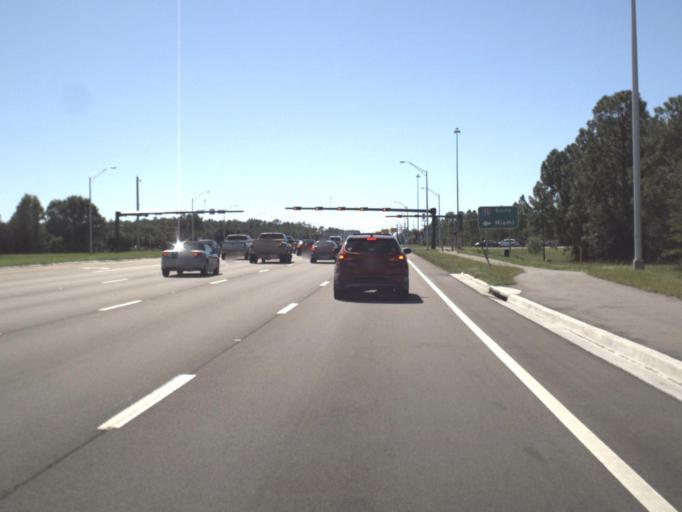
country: US
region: Florida
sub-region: Collier County
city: Golden Gate
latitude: 26.1602
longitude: -81.6868
